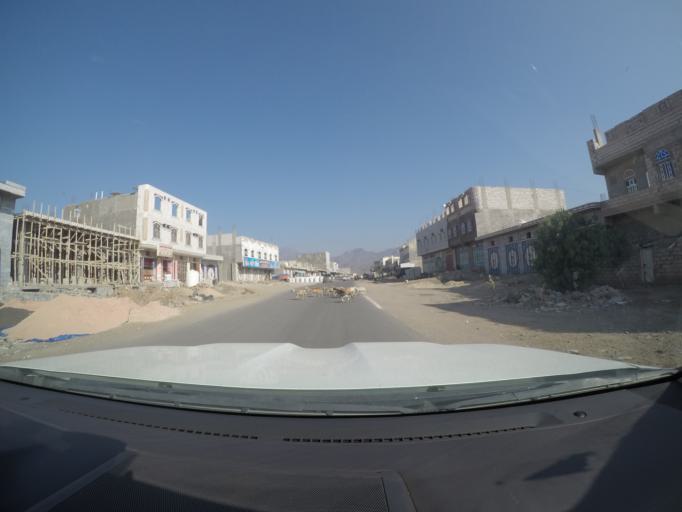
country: YE
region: Lahij
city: Habil ar Raydah
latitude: 13.6449
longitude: 44.8575
